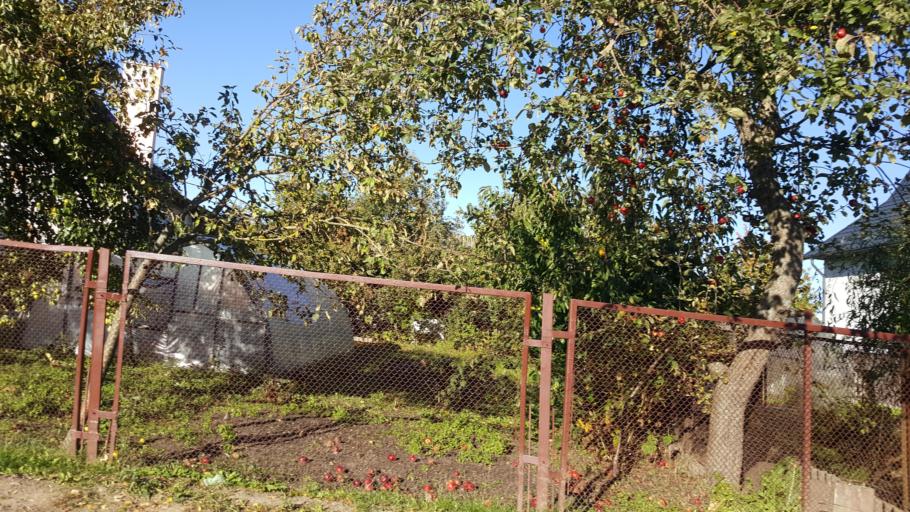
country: BY
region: Brest
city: Kamyanyets
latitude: 52.4015
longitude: 23.8296
